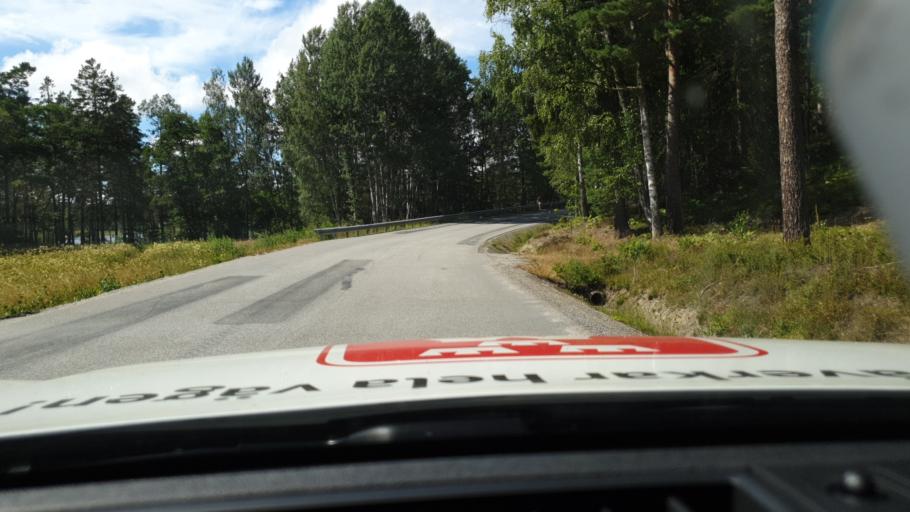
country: SE
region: Stockholm
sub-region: Haninge Kommun
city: Jordbro
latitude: 59.0247
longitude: 18.1596
